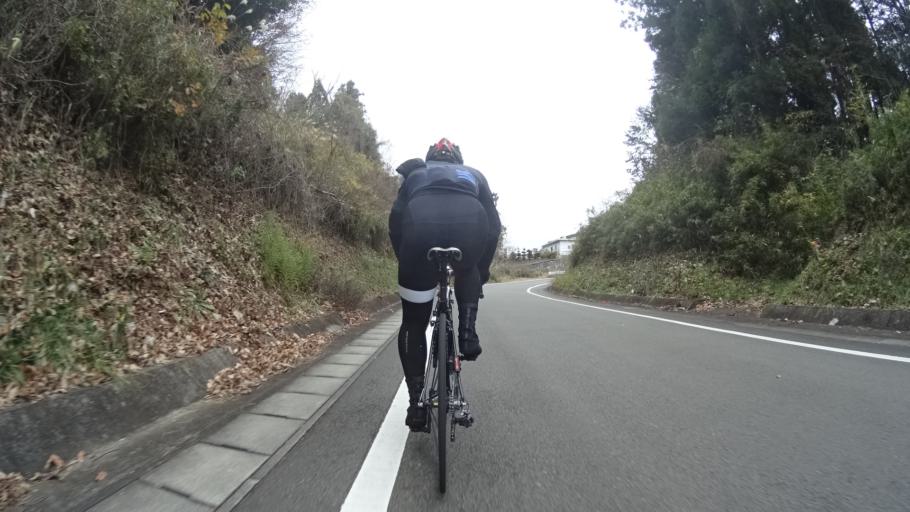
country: JP
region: Yamanashi
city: Otsuki
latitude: 35.6205
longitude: 138.9842
